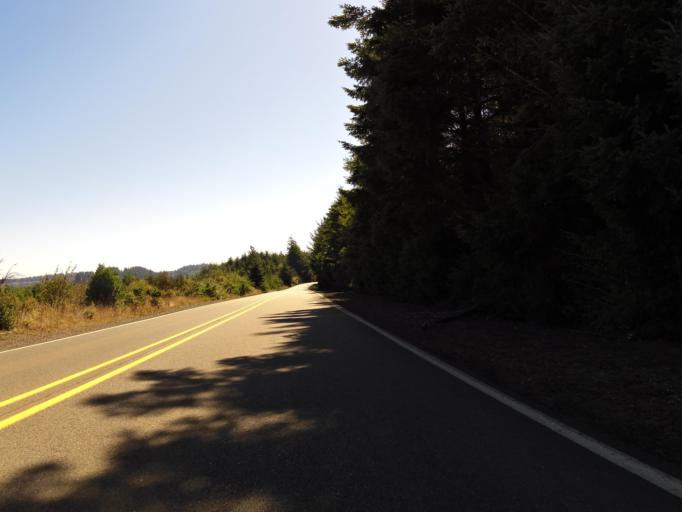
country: US
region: Oregon
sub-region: Coos County
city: Barview
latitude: 43.2451
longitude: -124.3333
